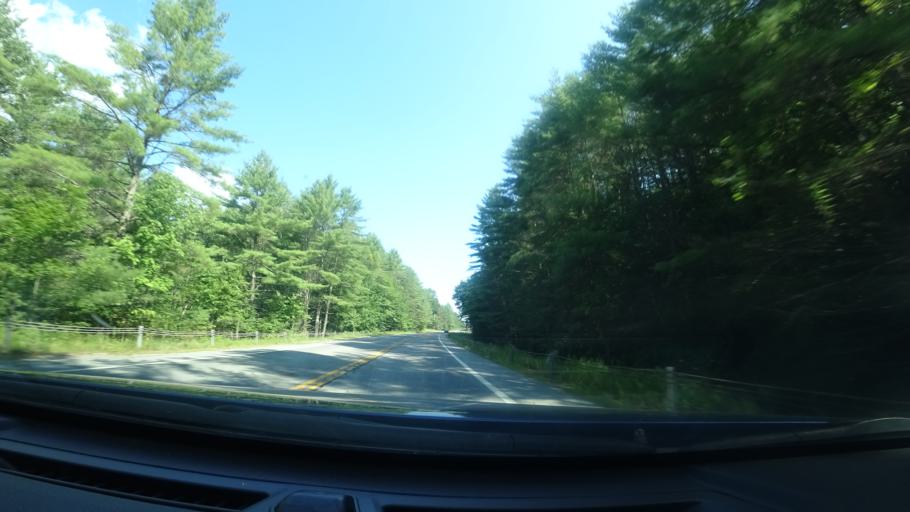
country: US
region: New York
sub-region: Warren County
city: Warrensburg
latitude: 43.6063
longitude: -73.8034
